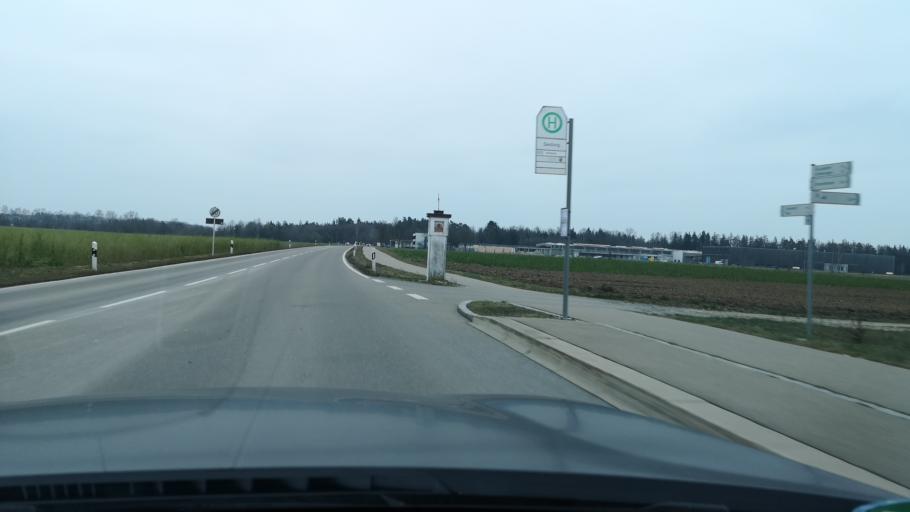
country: DE
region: Bavaria
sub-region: Swabia
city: Nersingen
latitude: 48.4274
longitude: 10.1653
